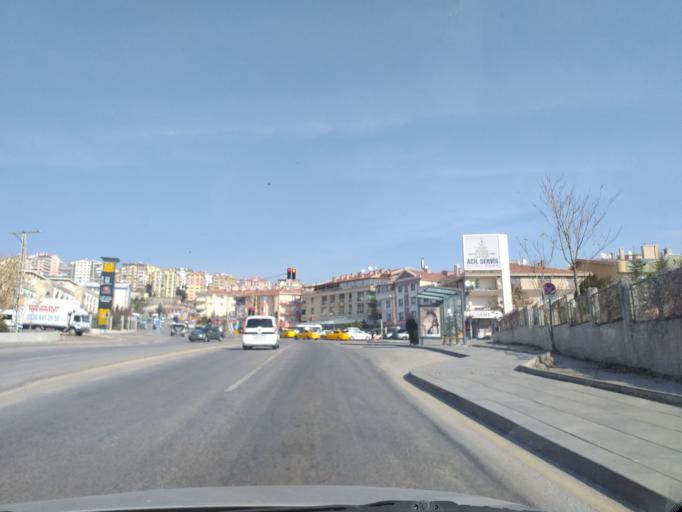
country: TR
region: Ankara
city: Mamak
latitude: 40.0032
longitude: 32.8558
